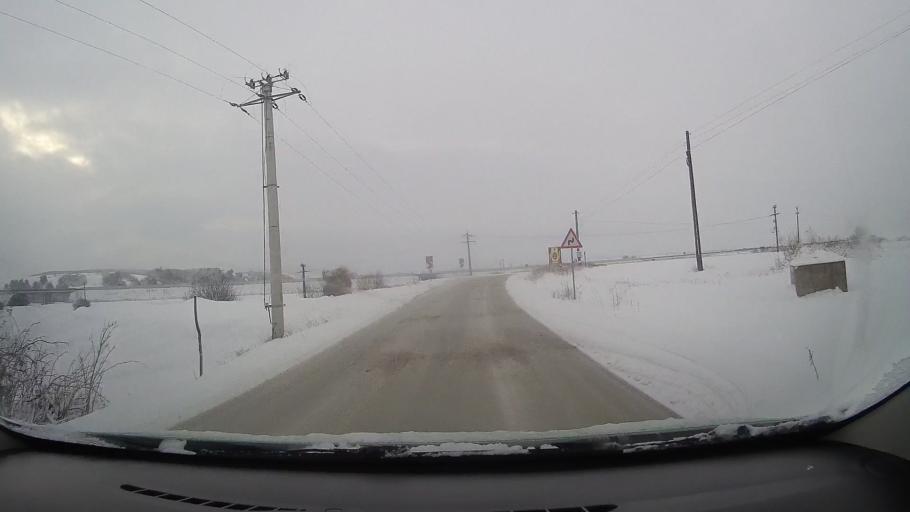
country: RO
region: Alba
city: Vurpar
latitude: 45.9711
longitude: 23.4804
